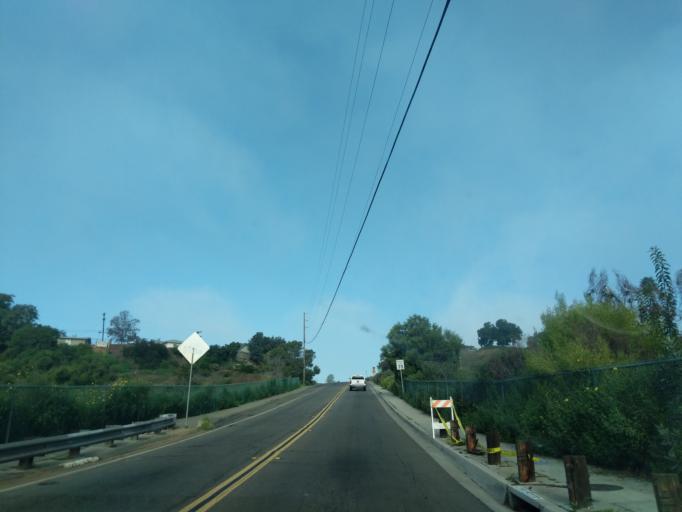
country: US
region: California
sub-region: San Diego County
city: Lemon Grove
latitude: 32.7359
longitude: -117.0878
